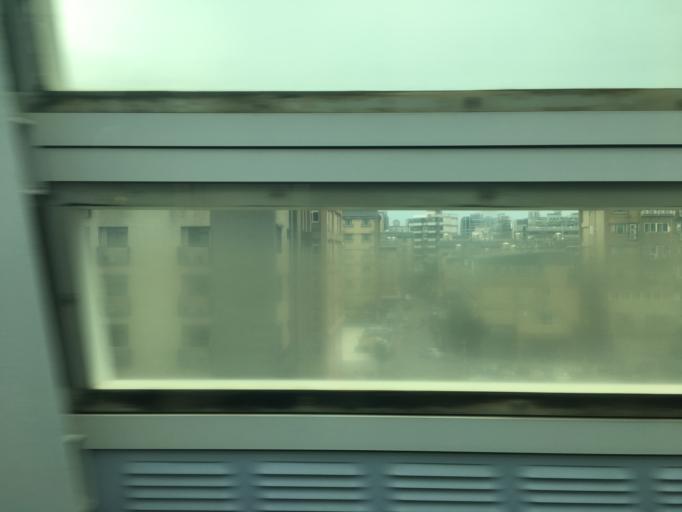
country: TW
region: Taiwan
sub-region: Taoyuan
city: Taoyuan
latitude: 25.0598
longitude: 121.3711
